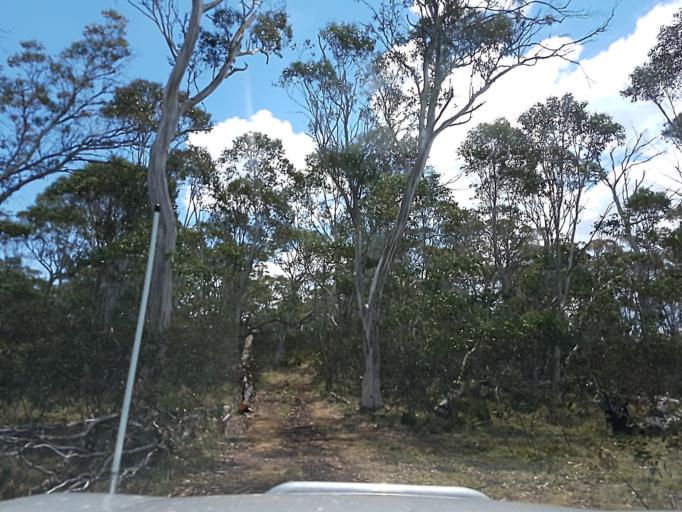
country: AU
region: New South Wales
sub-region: Snowy River
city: Jindabyne
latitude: -36.9154
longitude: 148.1313
